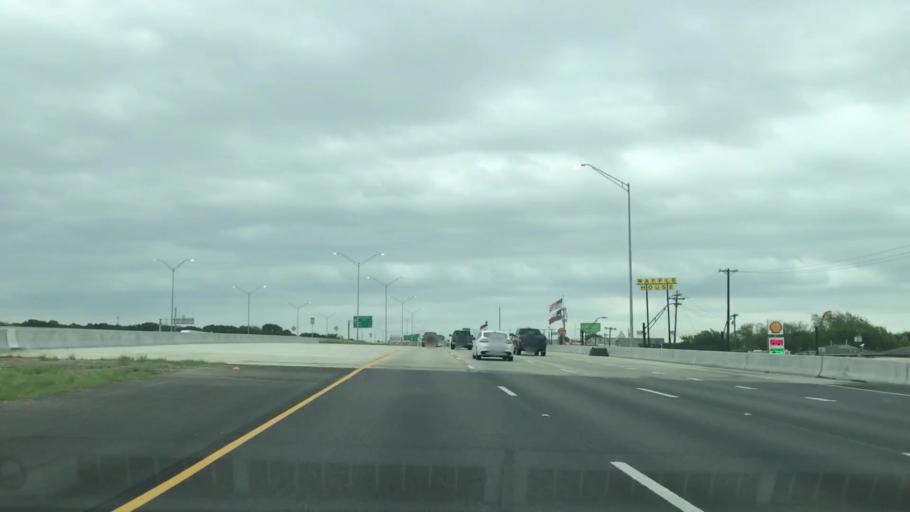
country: US
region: Texas
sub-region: Dallas County
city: Irving
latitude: 32.8369
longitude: -96.9521
